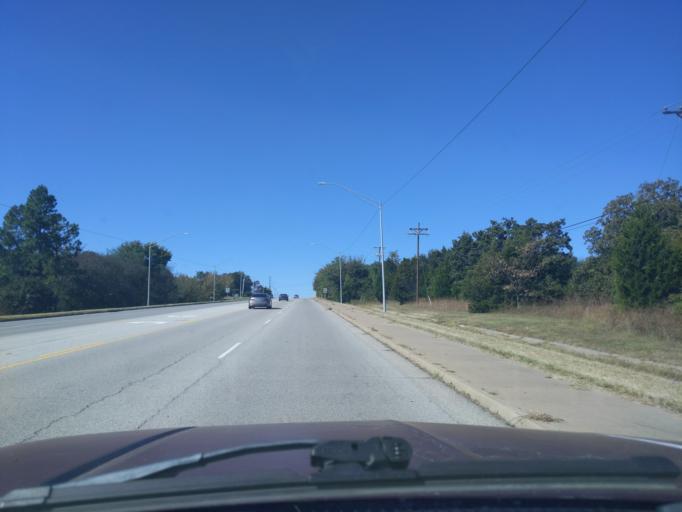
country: US
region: Oklahoma
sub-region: Creek County
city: Sapulpa
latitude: 35.9885
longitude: -96.0862
